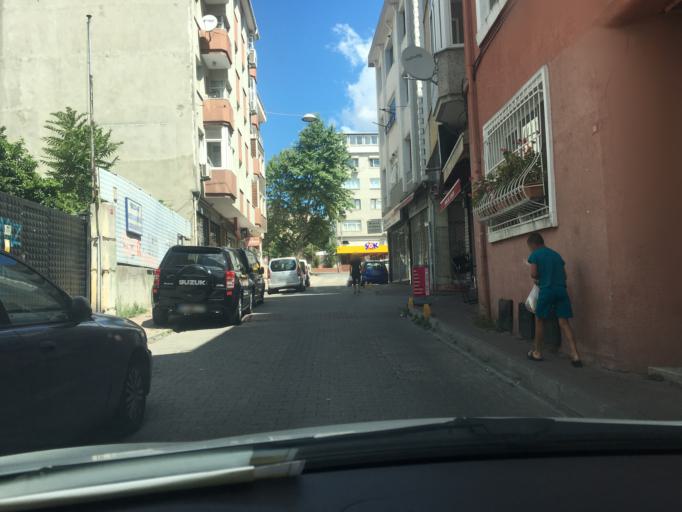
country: TR
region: Istanbul
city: Istanbul
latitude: 41.0038
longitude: 28.9338
